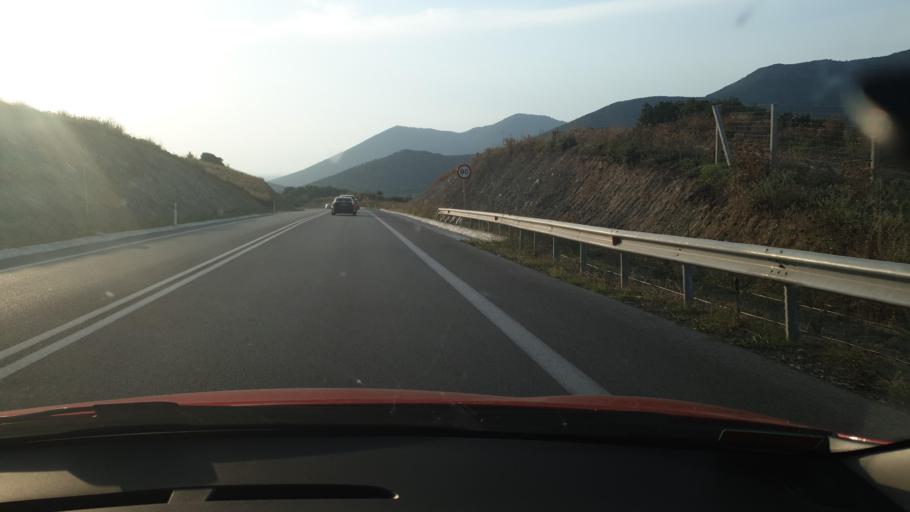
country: GR
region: Central Macedonia
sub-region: Nomos Chalkidikis
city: Galatista
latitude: 40.4629
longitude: 23.2215
